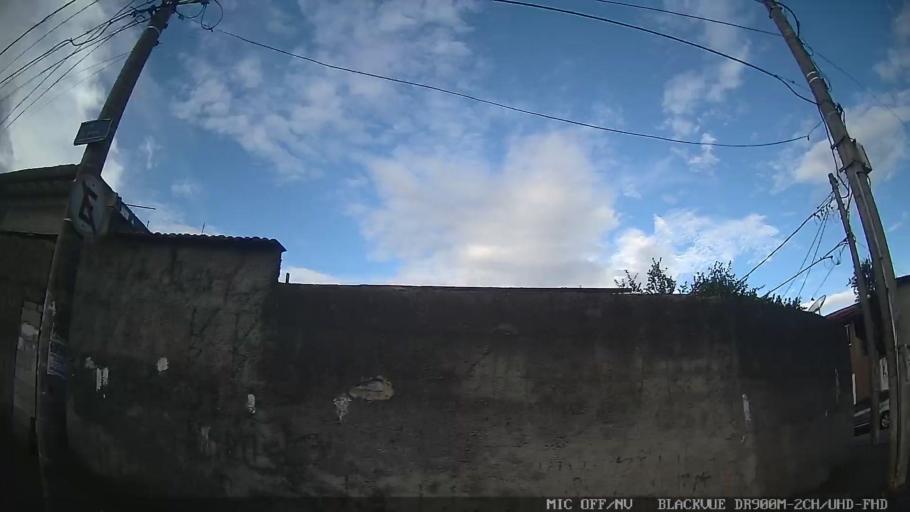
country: BR
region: Sao Paulo
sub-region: Mogi das Cruzes
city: Mogi das Cruzes
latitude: -23.5445
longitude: -46.2246
